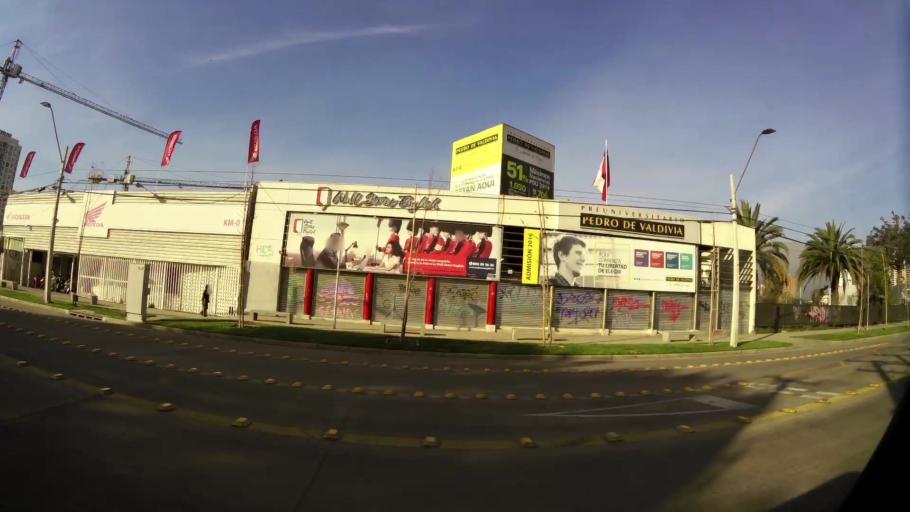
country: CL
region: Santiago Metropolitan
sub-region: Provincia de Santiago
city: Villa Presidente Frei, Nunoa, Santiago, Chile
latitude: -33.5183
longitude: -70.6041
